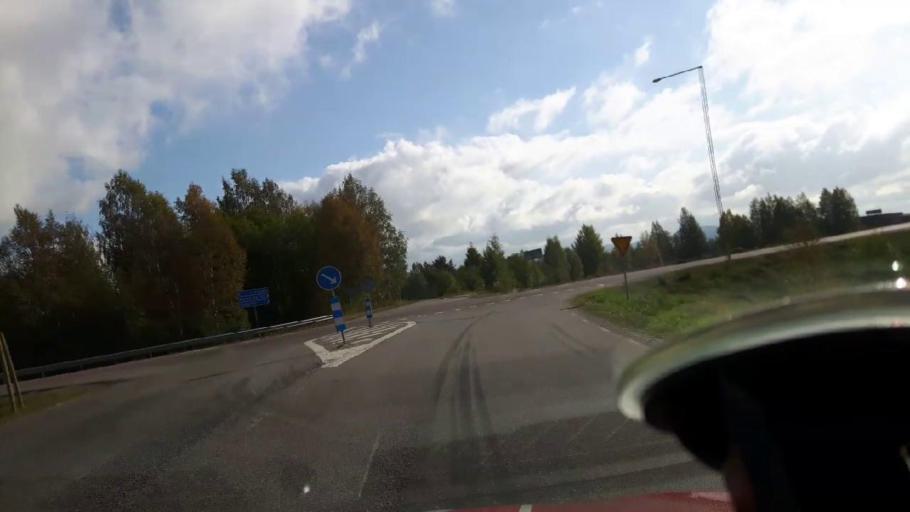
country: SE
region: Gaevleborg
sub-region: Ljusdals Kommun
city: Jaervsoe
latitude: 61.7512
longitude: 16.1593
